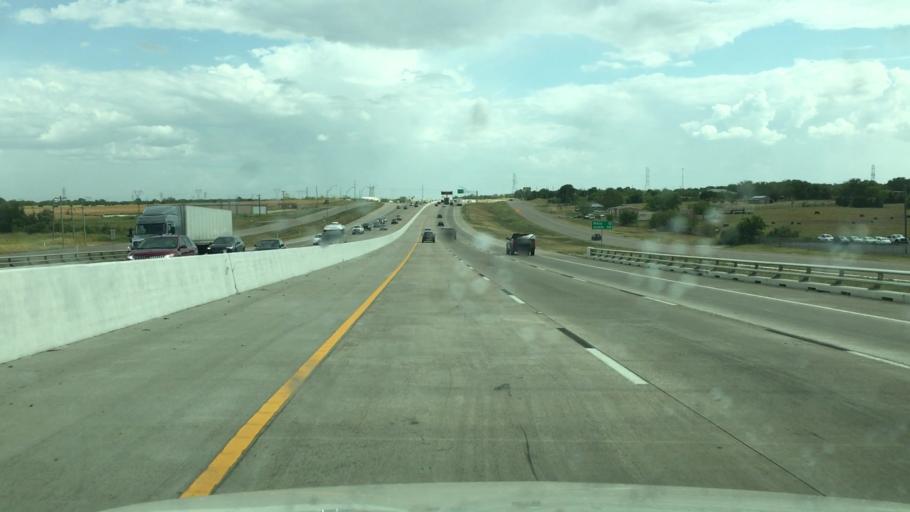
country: US
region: Texas
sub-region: McLennan County
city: Northcrest
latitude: 31.7132
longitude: -97.1024
